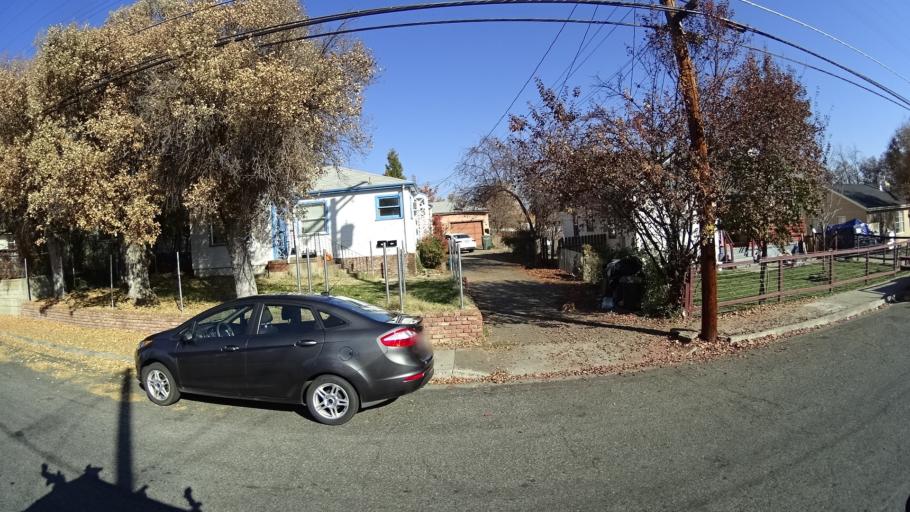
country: US
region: California
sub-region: Siskiyou County
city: Yreka
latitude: 41.7347
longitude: -122.6408
